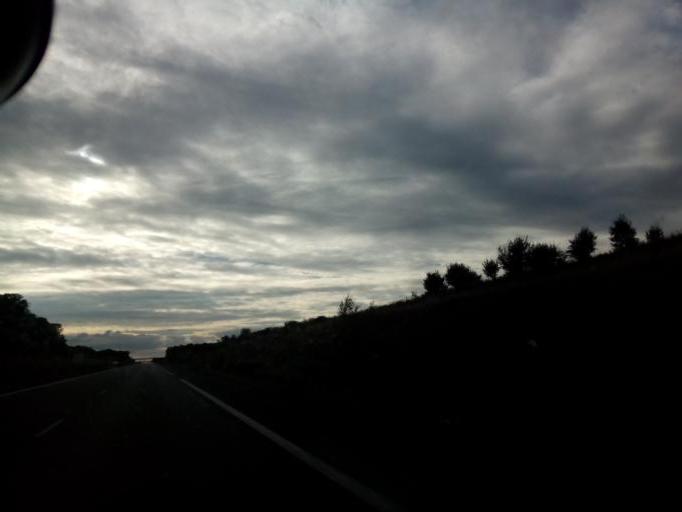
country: FR
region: Centre
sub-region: Departement d'Indre-et-Loire
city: Monts
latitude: 47.3069
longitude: 0.6276
